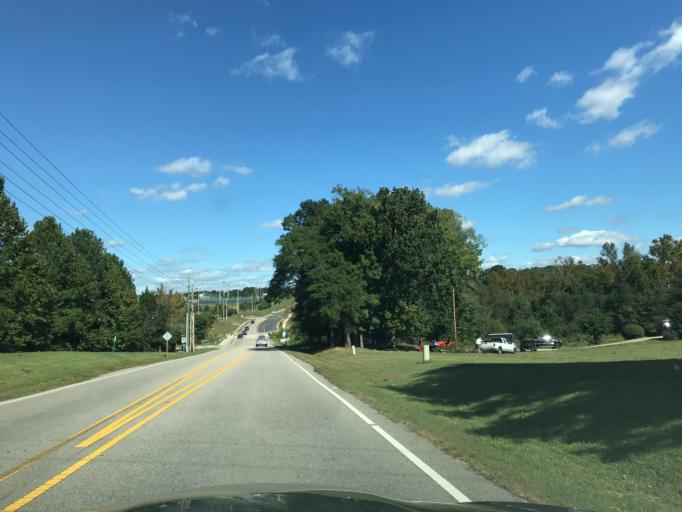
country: US
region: North Carolina
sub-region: Wake County
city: Wake Forest
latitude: 35.9358
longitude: -78.5069
